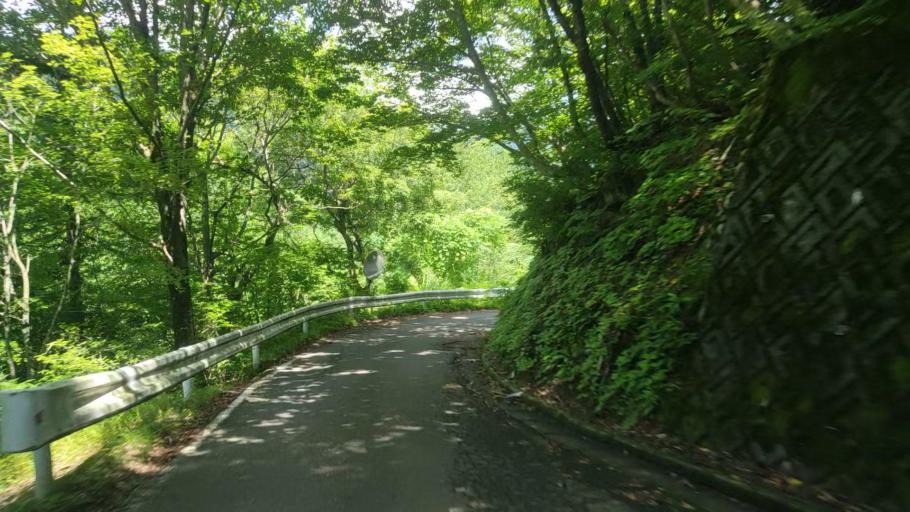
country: JP
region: Fukui
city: Ono
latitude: 35.7574
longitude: 136.5677
